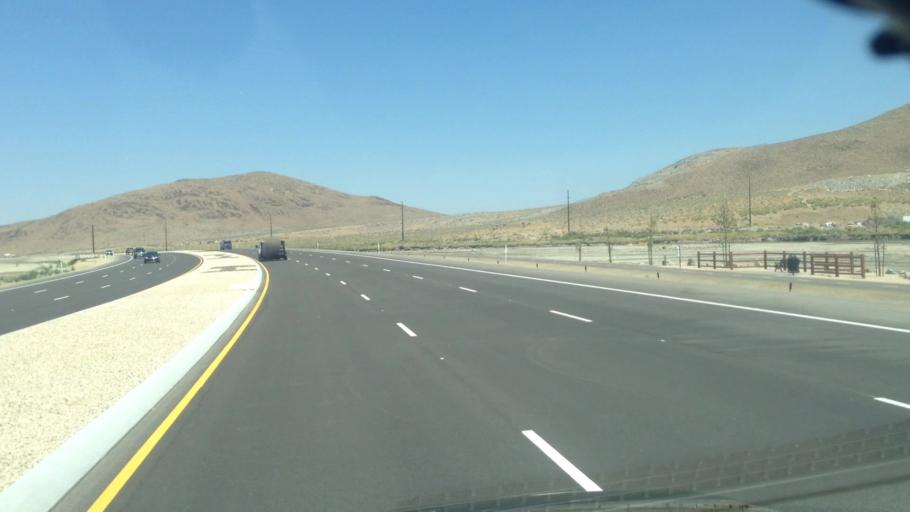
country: US
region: Nevada
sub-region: Washoe County
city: Sparks
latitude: 39.4578
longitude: -119.7248
